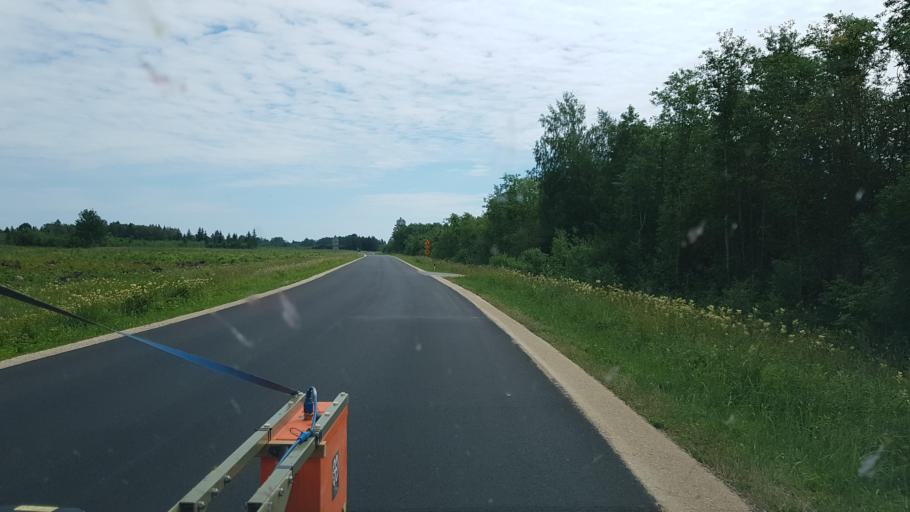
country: EE
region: Paernumaa
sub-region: Halinga vald
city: Parnu-Jaagupi
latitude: 58.6198
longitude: 24.2750
